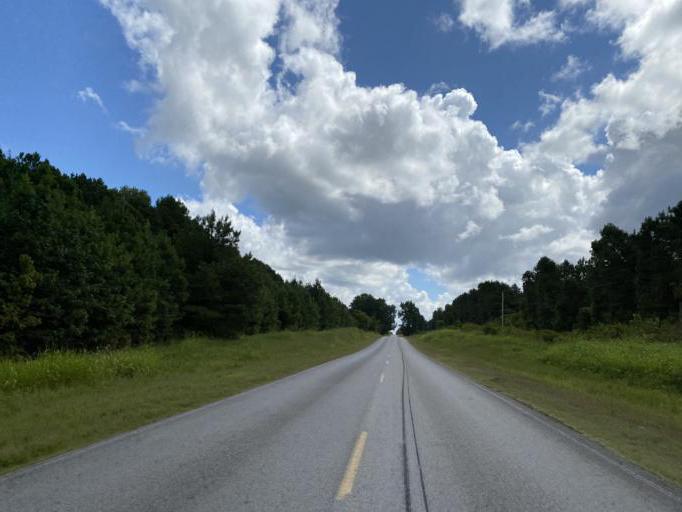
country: US
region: Mississippi
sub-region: Panola County
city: Como
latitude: 34.5105
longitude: -90.0207
